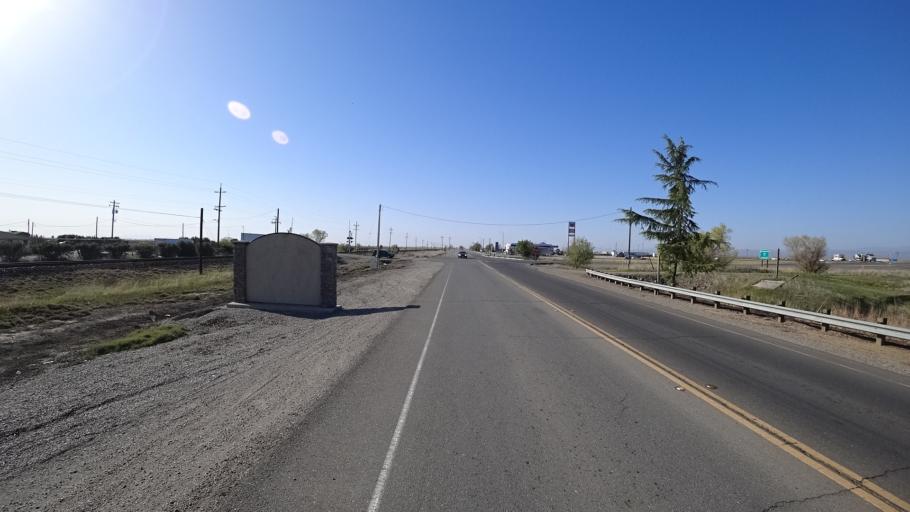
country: US
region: California
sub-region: Glenn County
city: Willows
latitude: 39.4956
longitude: -122.1932
